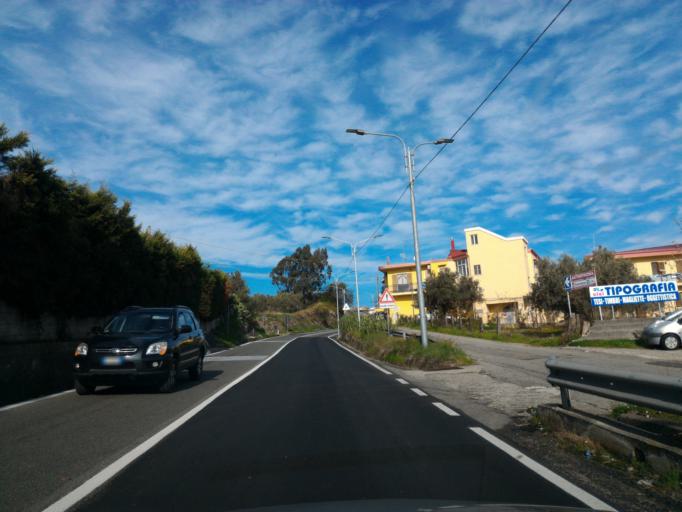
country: IT
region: Calabria
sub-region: Provincia di Catanzaro
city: Siano
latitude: 38.9084
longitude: 16.6020
